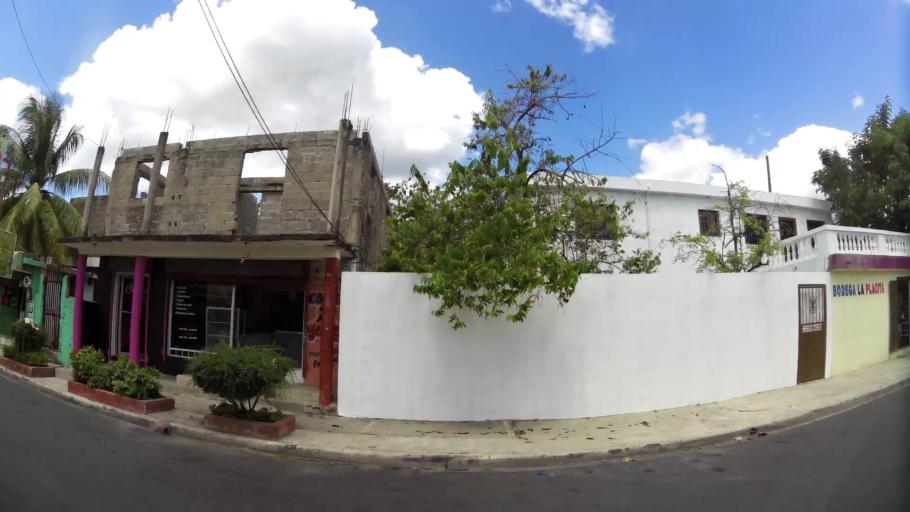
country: DO
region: Nacional
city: Ensanche Luperon
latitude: 18.5175
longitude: -69.9083
